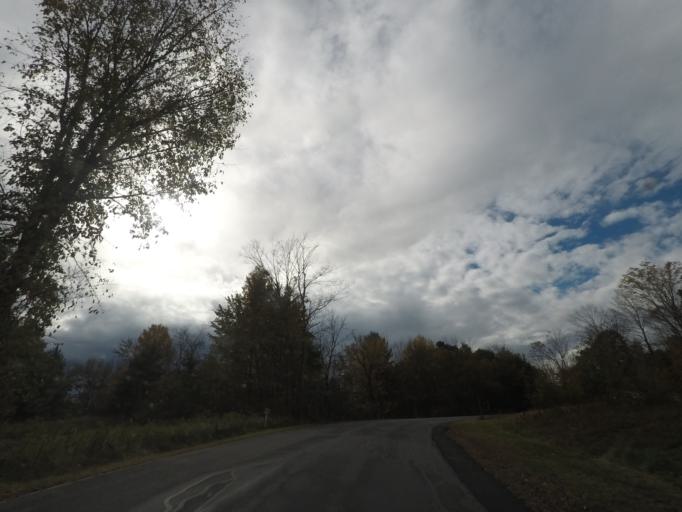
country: US
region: New York
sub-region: Rensselaer County
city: Nassau
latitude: 42.5765
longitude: -73.6312
